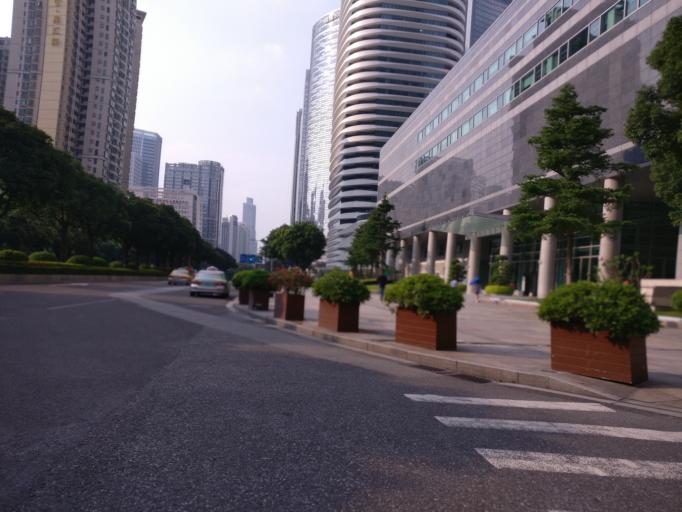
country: CN
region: Guangdong
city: Wushan
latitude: 23.1235
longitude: 113.3160
